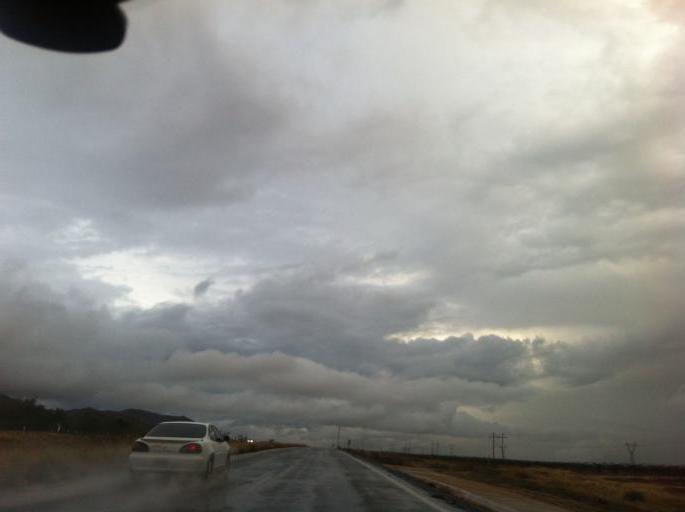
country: MX
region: Sonora
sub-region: San Miguel de Horcasitas
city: Las Mercedes [Agropecuaria]
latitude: 29.4527
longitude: -110.9913
